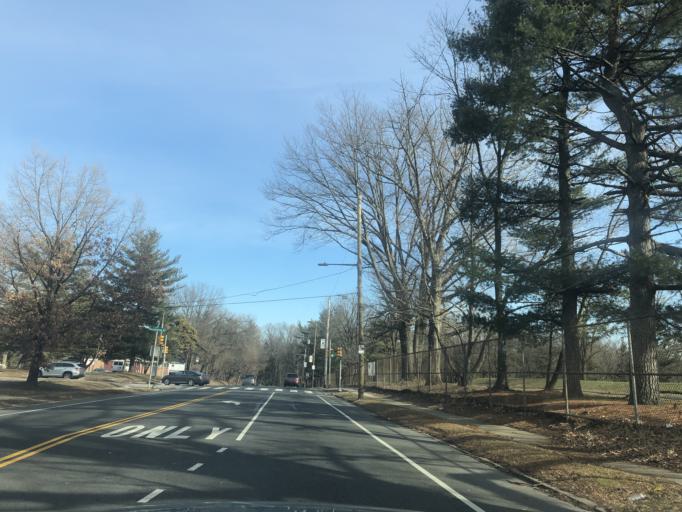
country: US
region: Pennsylvania
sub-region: Montgomery County
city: Bala-Cynwyd
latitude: 40.0294
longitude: -75.2040
